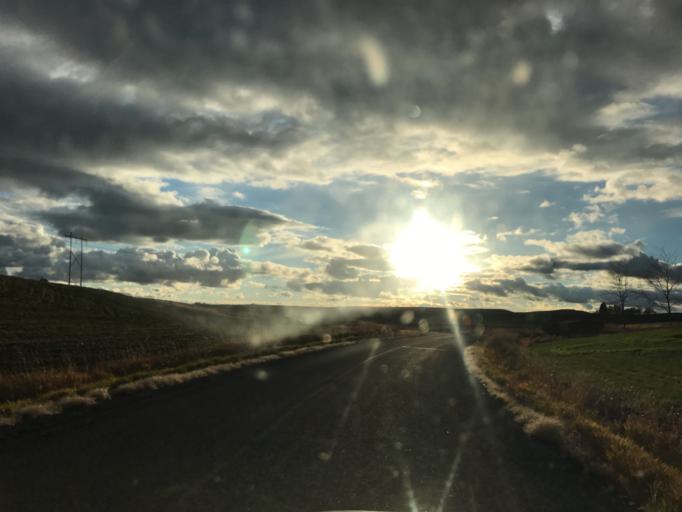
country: US
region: Idaho
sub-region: Latah County
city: Moscow
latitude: 46.7738
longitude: -116.9691
